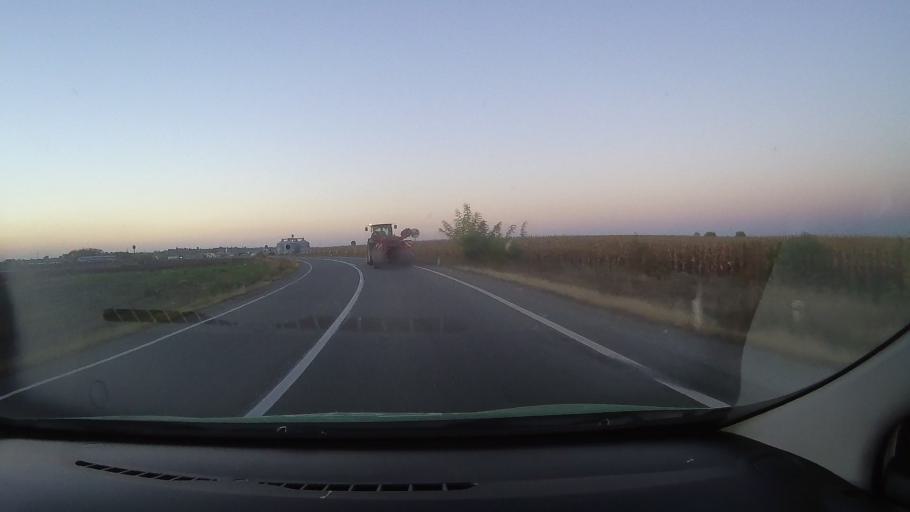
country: RO
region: Bihor
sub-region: Comuna Tarcea
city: Tarcea
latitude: 47.4491
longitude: 22.1854
